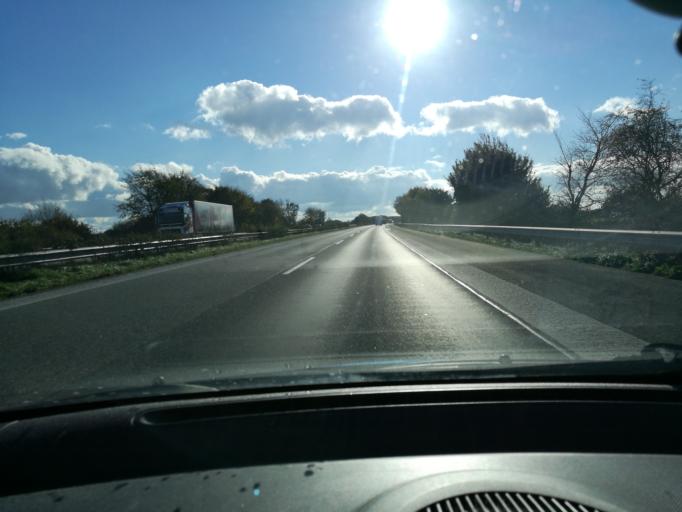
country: DE
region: Schleswig-Holstein
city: Lottorf
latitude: 54.4536
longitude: 9.5817
